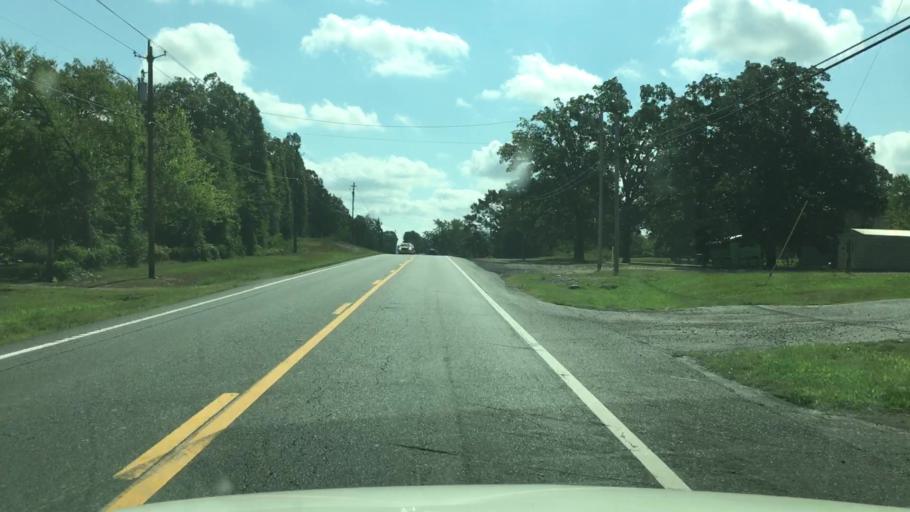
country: US
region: Arkansas
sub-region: Garland County
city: Piney
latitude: 34.5094
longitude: -93.1607
